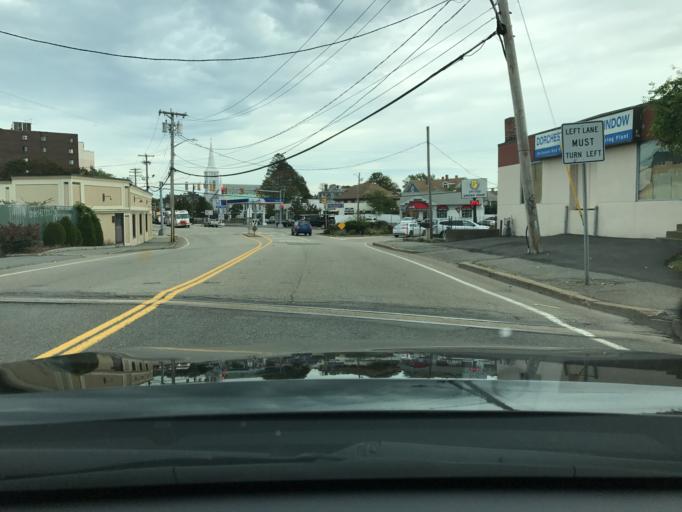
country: US
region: Massachusetts
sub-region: Norfolk County
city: Quincy
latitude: 42.2438
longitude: -71.0044
